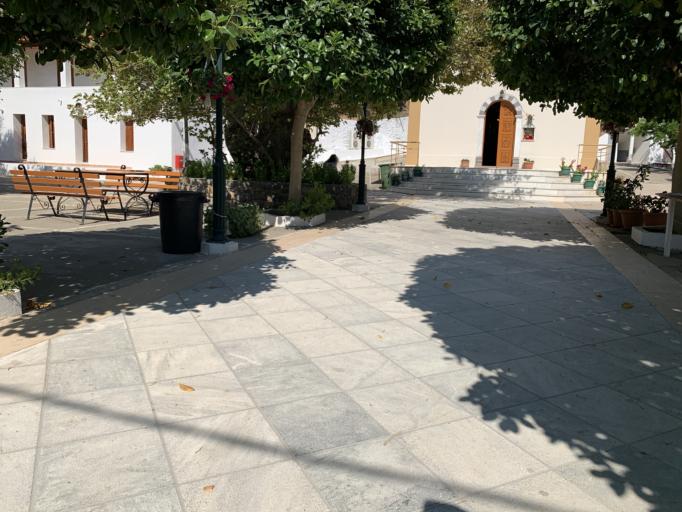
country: GR
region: North Aegean
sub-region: Chios
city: Vrontados
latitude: 38.4800
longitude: 25.8871
